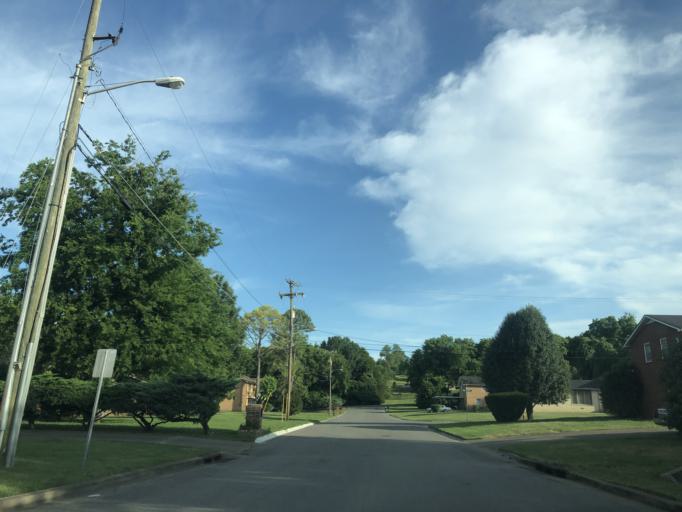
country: US
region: Tennessee
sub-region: Davidson County
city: Nashville
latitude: 36.2186
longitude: -86.8513
